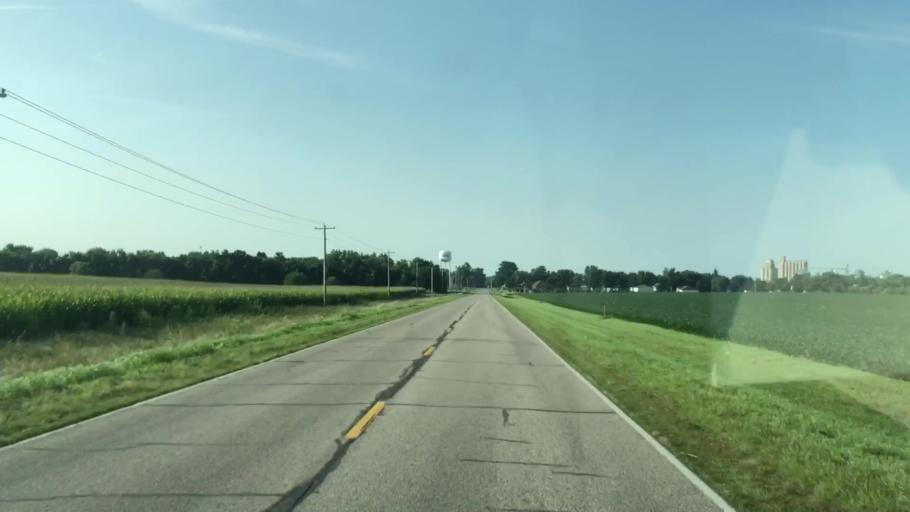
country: US
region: Iowa
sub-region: Lyon County
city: George
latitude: 43.3523
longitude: -95.9984
